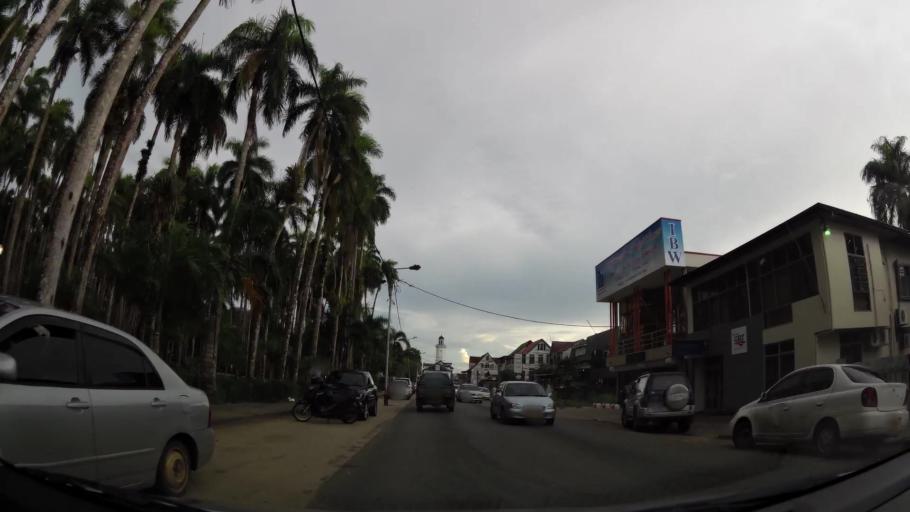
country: SR
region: Paramaribo
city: Paramaribo
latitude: 5.8290
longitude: -55.1509
